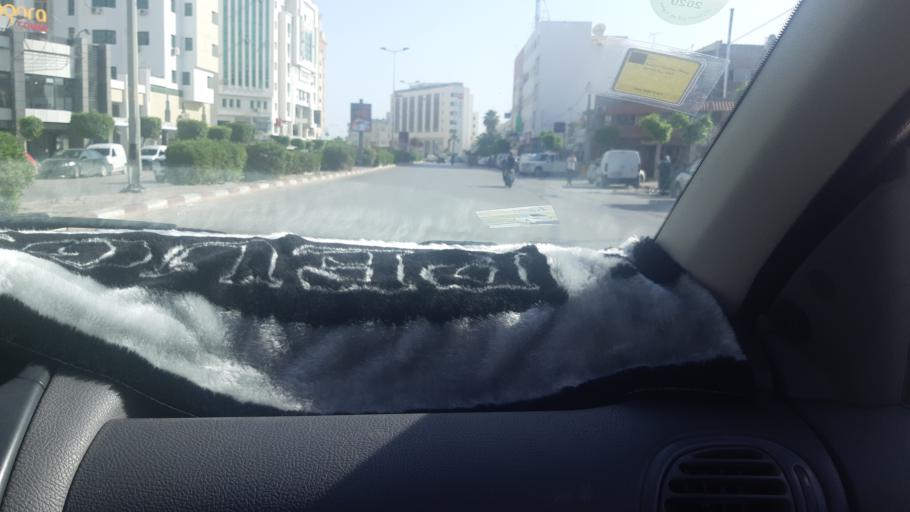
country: TN
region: Safaqis
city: Sfax
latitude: 34.7390
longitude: 10.7505
